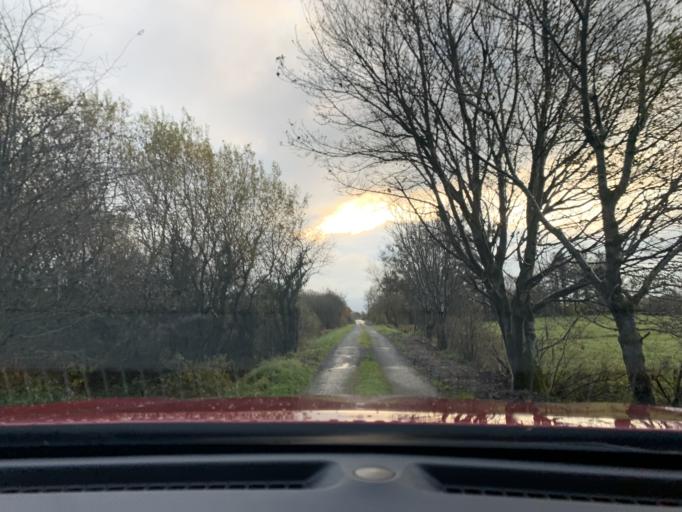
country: IE
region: Connaught
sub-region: Sligo
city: Ballymote
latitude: 54.0324
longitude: -8.5319
